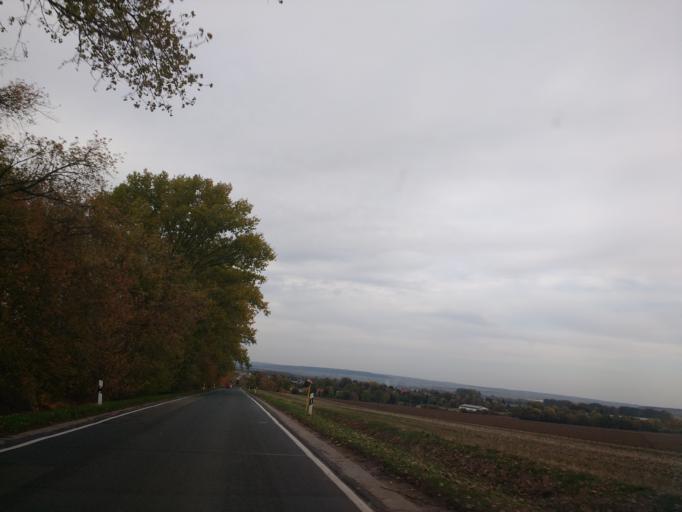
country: DE
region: Thuringia
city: Seebach
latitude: 51.1569
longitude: 10.5179
